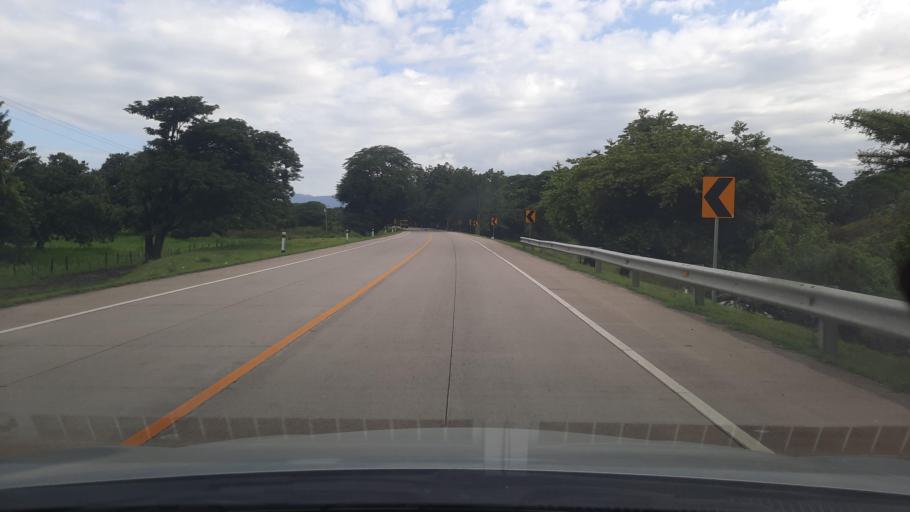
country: NI
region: Chinandega
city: Somotillo
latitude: 12.8302
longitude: -86.8963
